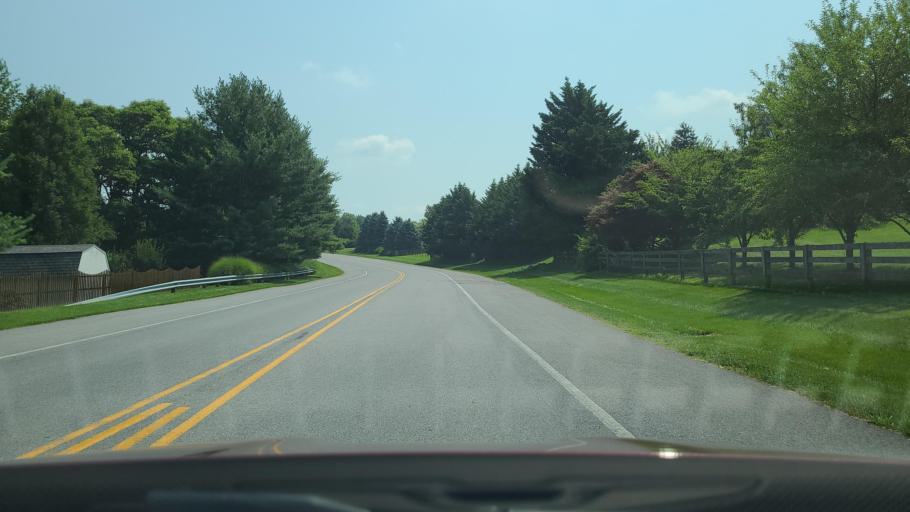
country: US
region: Maryland
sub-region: Frederick County
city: Jefferson
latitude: 39.3642
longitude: -77.5280
